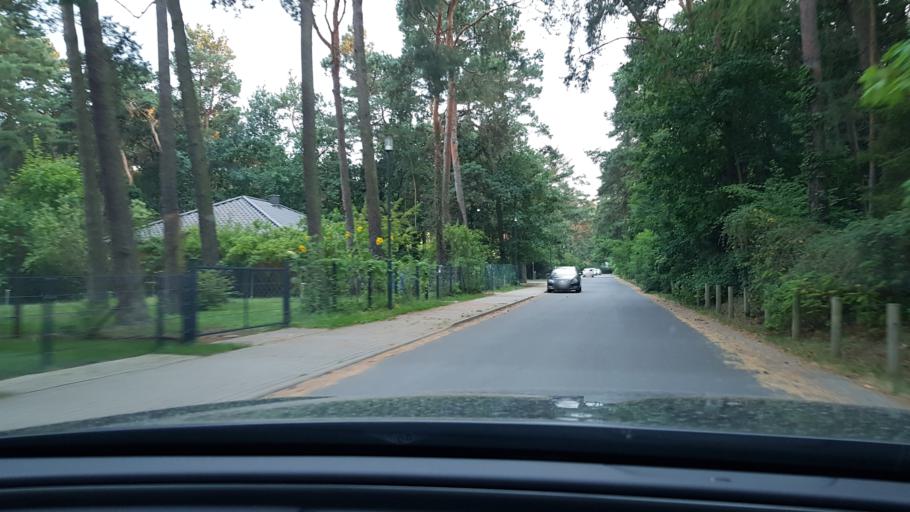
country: DE
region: Berlin
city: Friedrichshagen
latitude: 52.4802
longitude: 13.6281
